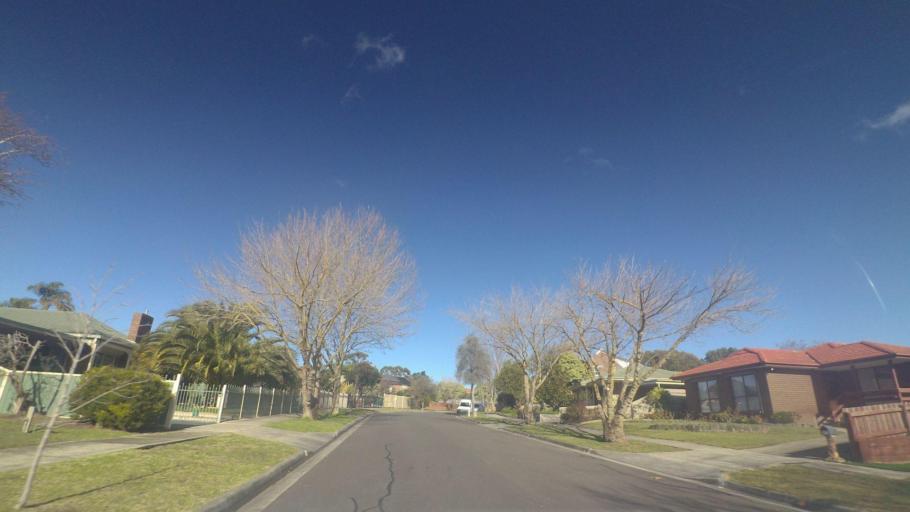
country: AU
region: Victoria
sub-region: Knox
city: Rowville
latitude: -37.9202
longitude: 145.2519
